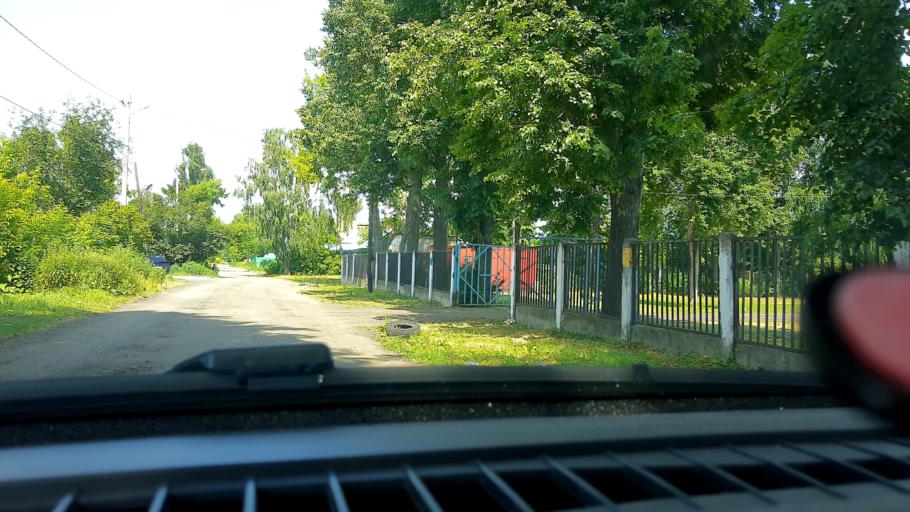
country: RU
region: Nizjnij Novgorod
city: Gorbatovka
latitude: 56.2705
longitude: 43.7517
